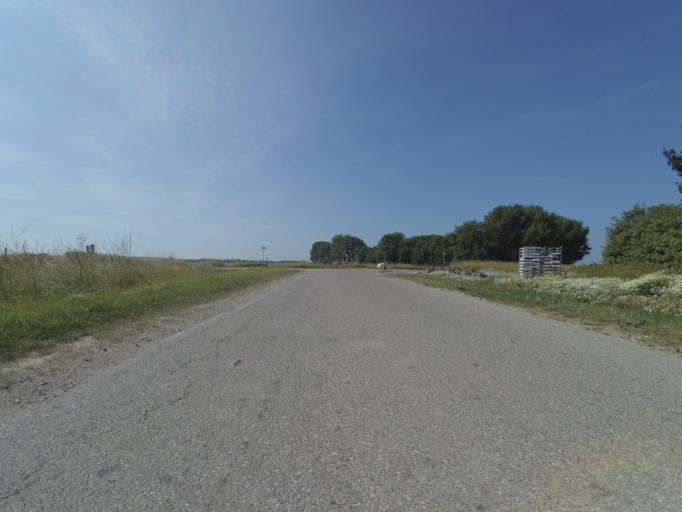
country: NL
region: North Brabant
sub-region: Gemeente Steenbergen
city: Nieuw-Vossemeer
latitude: 51.6038
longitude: 4.2130
